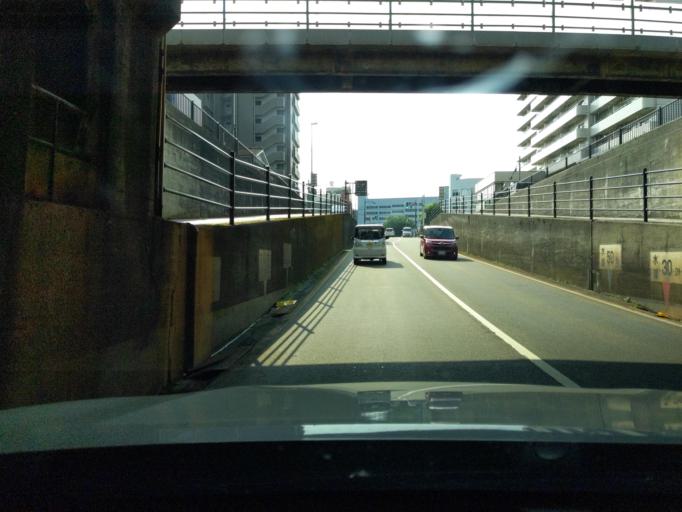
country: JP
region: Niigata
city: Nagaoka
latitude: 37.4428
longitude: 138.8521
